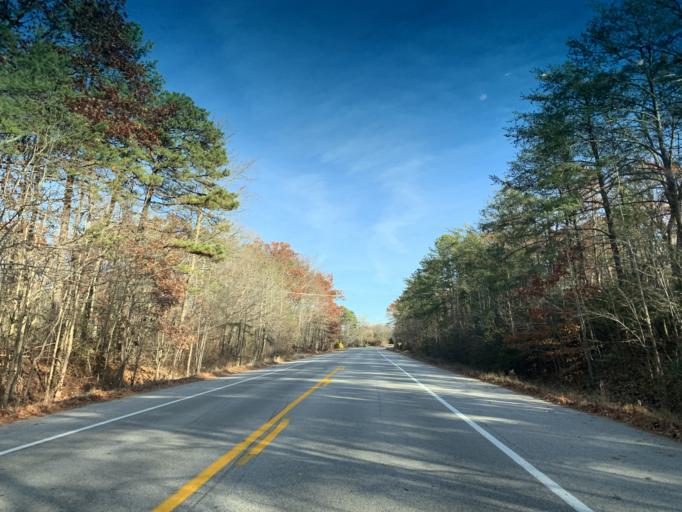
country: US
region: Maryland
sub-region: Cecil County
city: Charlestown
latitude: 39.5748
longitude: -75.9900
